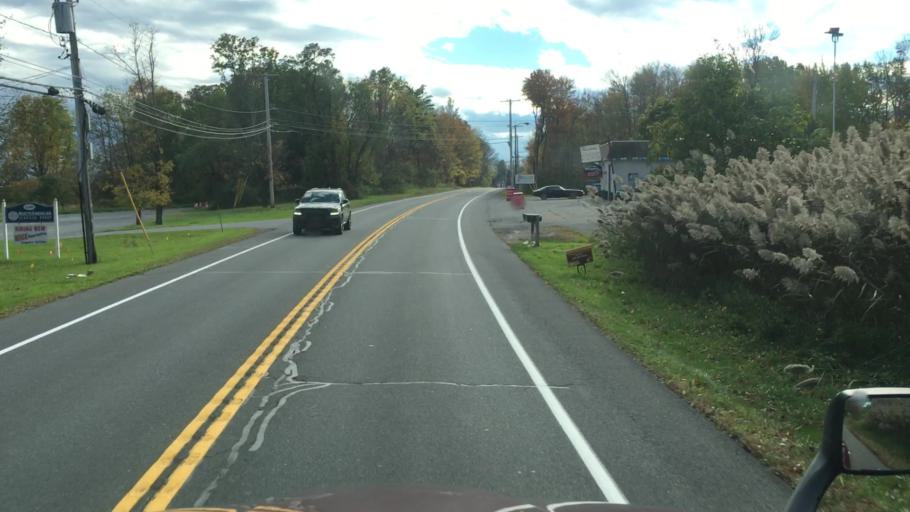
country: US
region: New York
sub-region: Saratoga County
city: Ballston Spa
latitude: 42.9625
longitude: -73.8635
